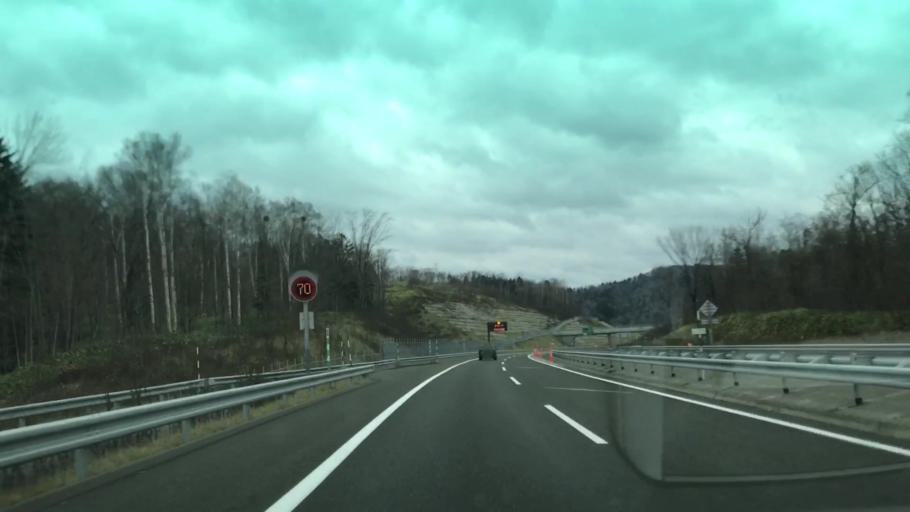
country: JP
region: Hokkaido
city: Shimo-furano
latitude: 42.9868
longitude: 142.4119
